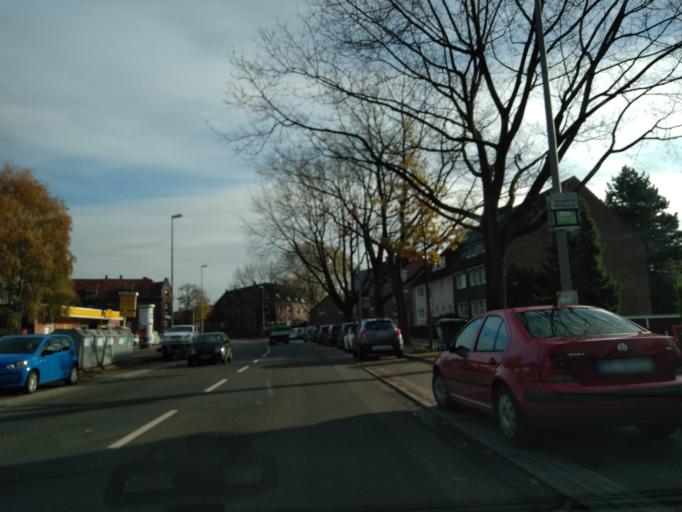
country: DE
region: North Rhine-Westphalia
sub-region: Regierungsbezirk Munster
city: Gladbeck
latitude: 51.5782
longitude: 6.9605
